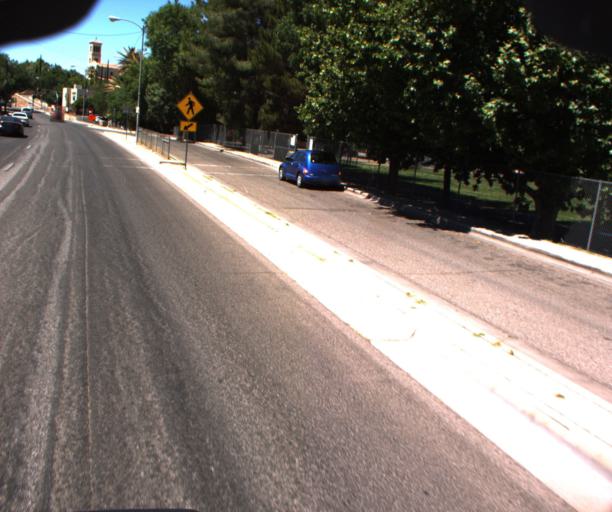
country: US
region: Arizona
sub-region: Santa Cruz County
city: Nogales
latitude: 31.3399
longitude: -110.9391
